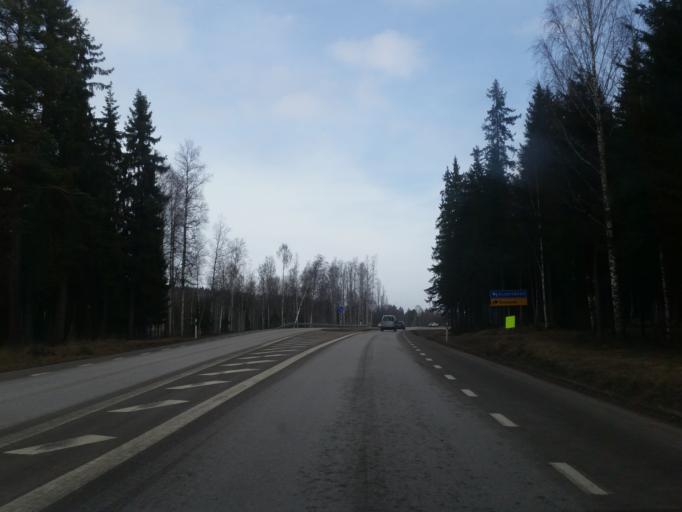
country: SE
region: Dalarna
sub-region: Leksand Municipality
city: Leksand
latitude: 60.7890
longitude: 15.0350
